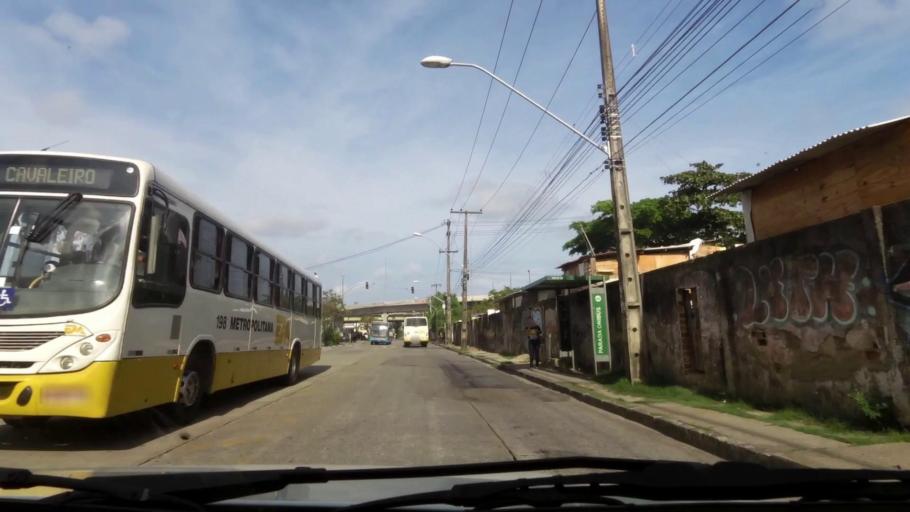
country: BR
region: Pernambuco
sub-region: Recife
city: Recife
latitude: -8.0757
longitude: -34.8912
